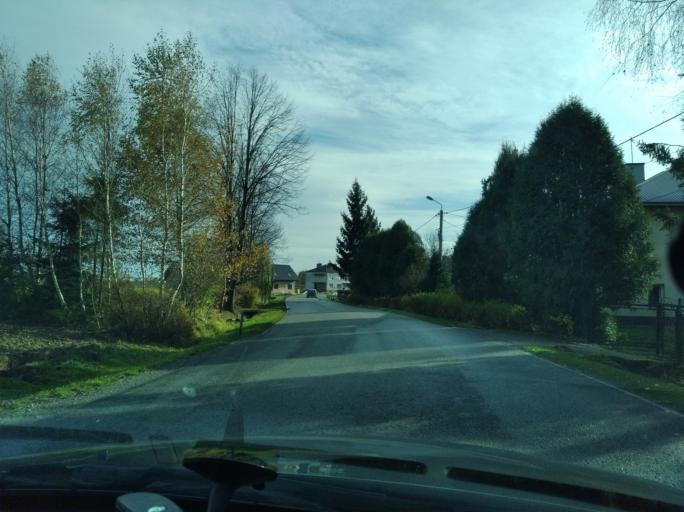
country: PL
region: Subcarpathian Voivodeship
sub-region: Powiat ropczycko-sedziszowski
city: Sedziszow Malopolski
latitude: 50.0902
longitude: 21.7451
